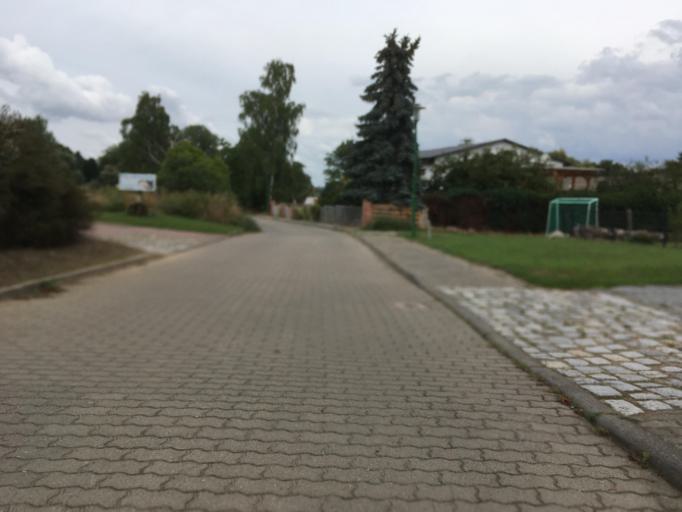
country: DE
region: Brandenburg
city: Prenzlau
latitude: 53.2637
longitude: 13.8492
